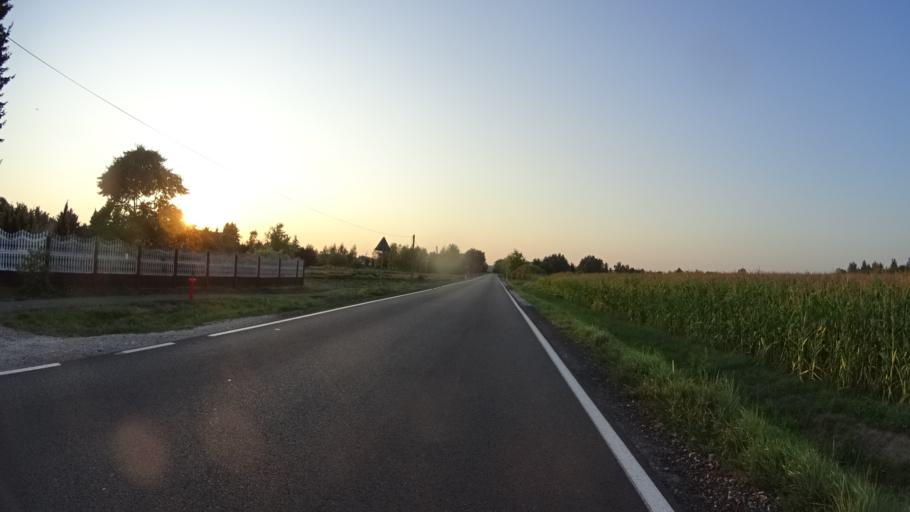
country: PL
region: Masovian Voivodeship
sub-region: Powiat warszawski zachodni
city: Ozarow Mazowiecki
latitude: 52.2474
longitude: 20.7445
